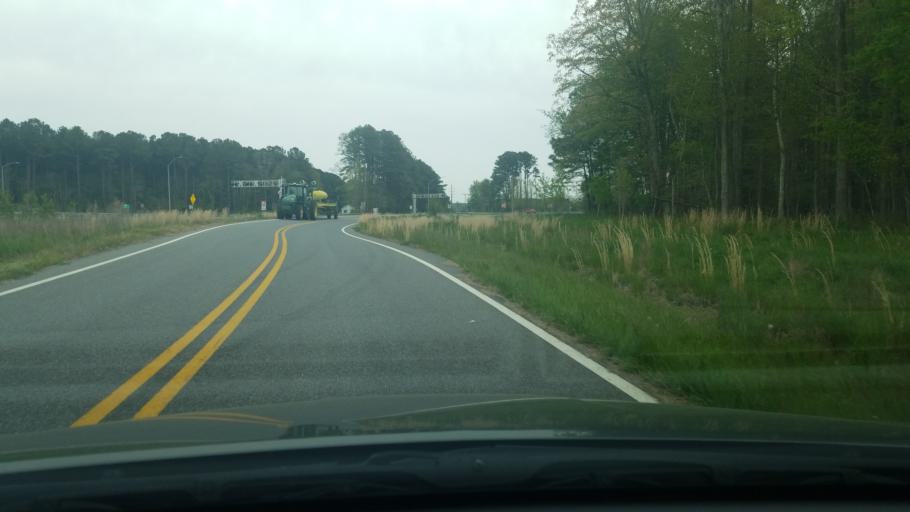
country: US
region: Maryland
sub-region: Worcester County
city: Snow Hill
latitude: 38.2428
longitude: -75.3021
